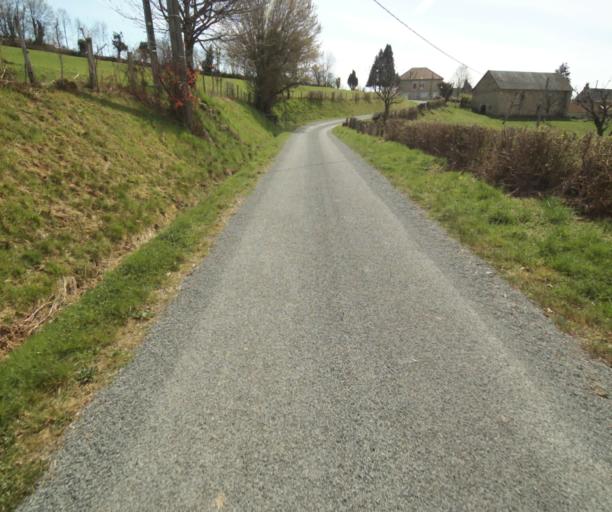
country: FR
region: Limousin
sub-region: Departement de la Correze
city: Naves
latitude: 45.3786
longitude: 1.8006
